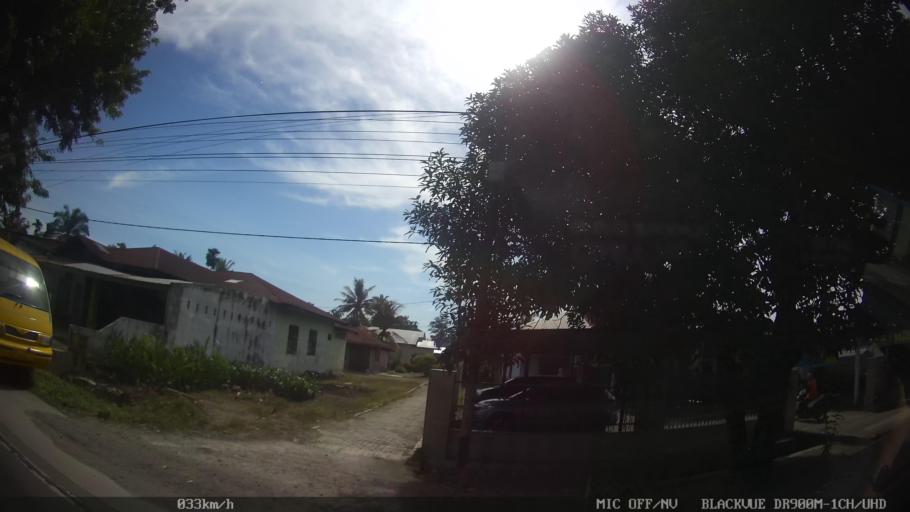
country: ID
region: North Sumatra
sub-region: Kabupaten Langkat
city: Stabat
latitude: 3.7074
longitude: 98.5060
